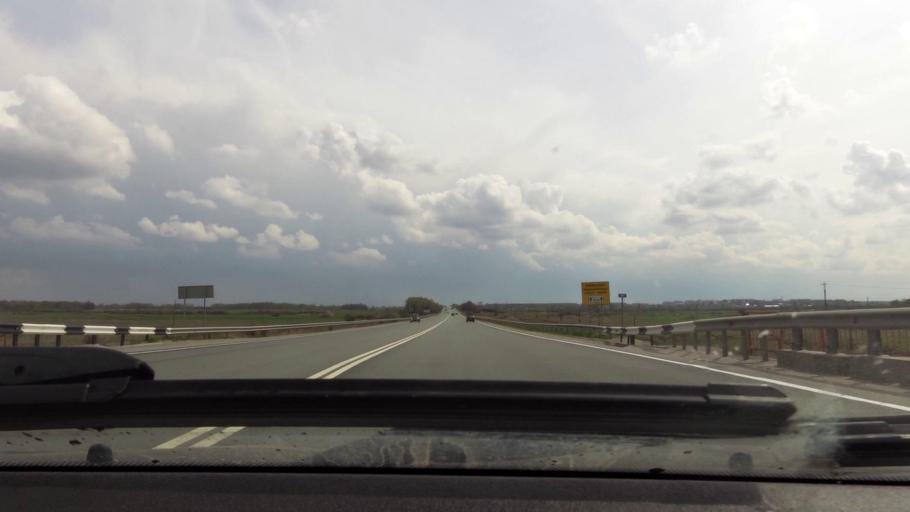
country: RU
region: Rjazan
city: Bagramovo
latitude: 54.7434
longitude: 39.4386
